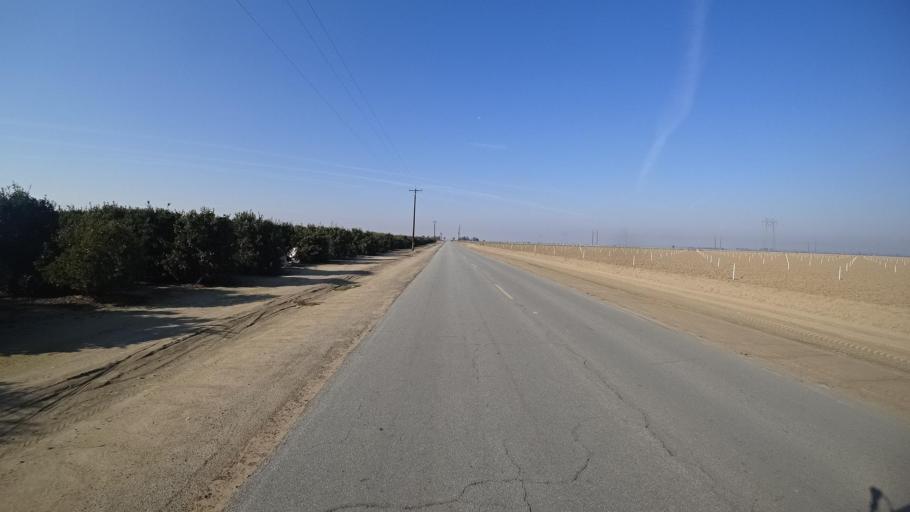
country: US
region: California
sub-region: Kern County
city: Weedpatch
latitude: 35.1220
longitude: -118.9728
